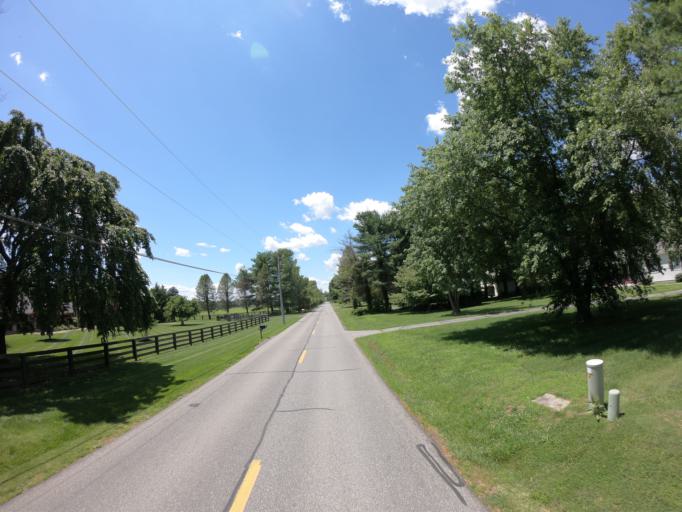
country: US
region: Delaware
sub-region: New Castle County
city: Middletown
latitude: 39.4805
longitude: -75.7425
